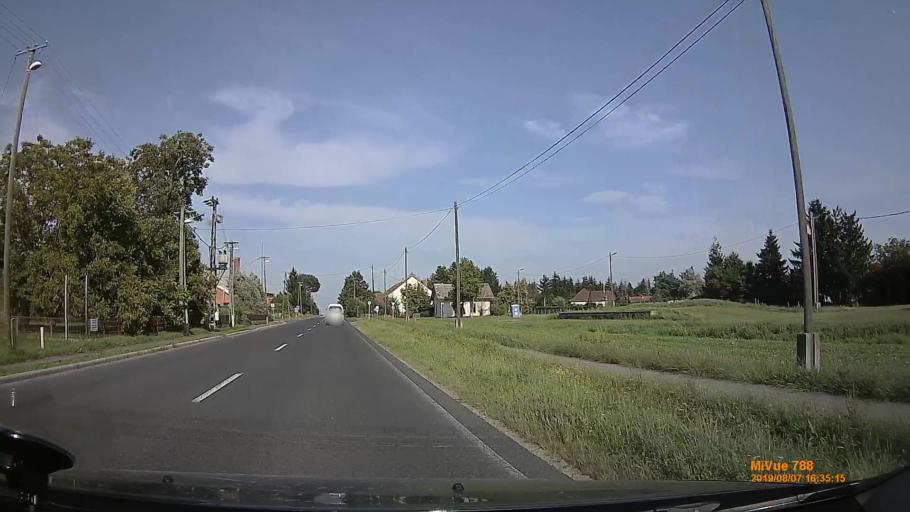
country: SI
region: Lendava-Lendva
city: Lendava
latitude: 46.6182
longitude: 16.4693
